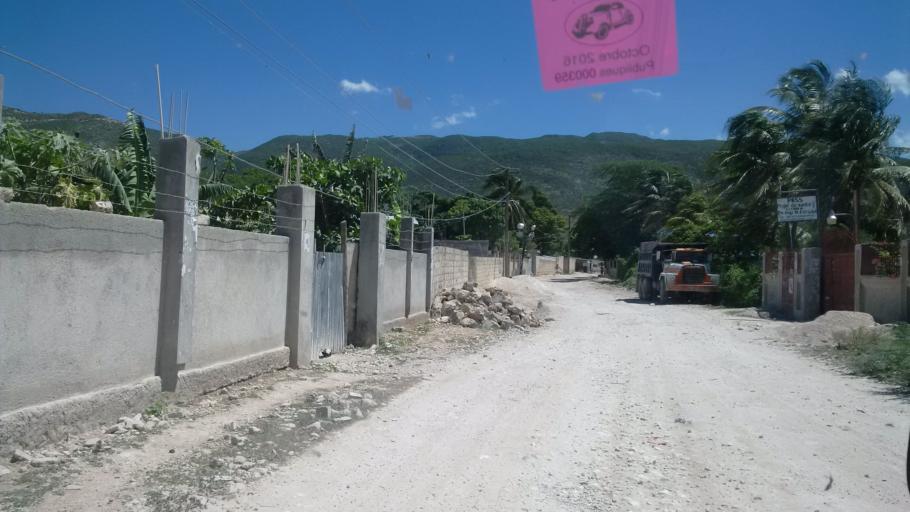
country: HT
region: Ouest
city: Thomazeau
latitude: 18.6561
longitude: -72.1513
